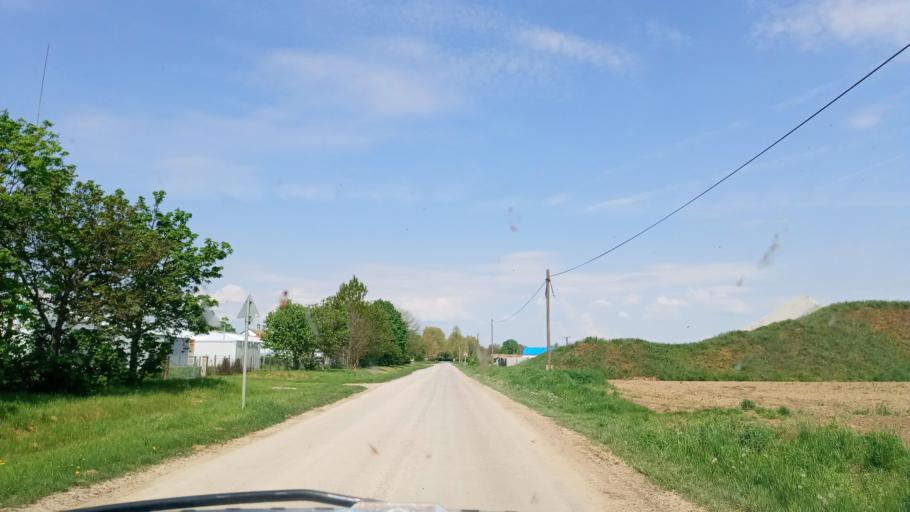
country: HU
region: Baranya
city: Boly
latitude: 45.9087
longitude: 18.5493
